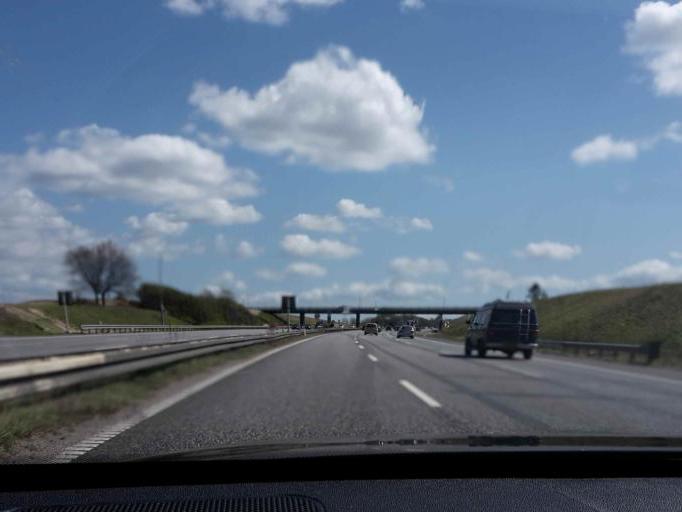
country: DK
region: South Denmark
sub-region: Middelfart Kommune
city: Strib
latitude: 55.5144
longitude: 9.7698
